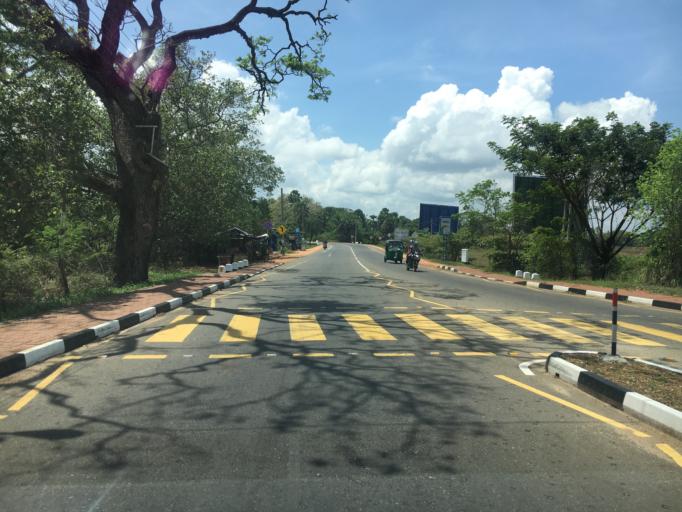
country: LK
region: North Central
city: Anuradhapura
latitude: 8.2740
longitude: 80.5002
